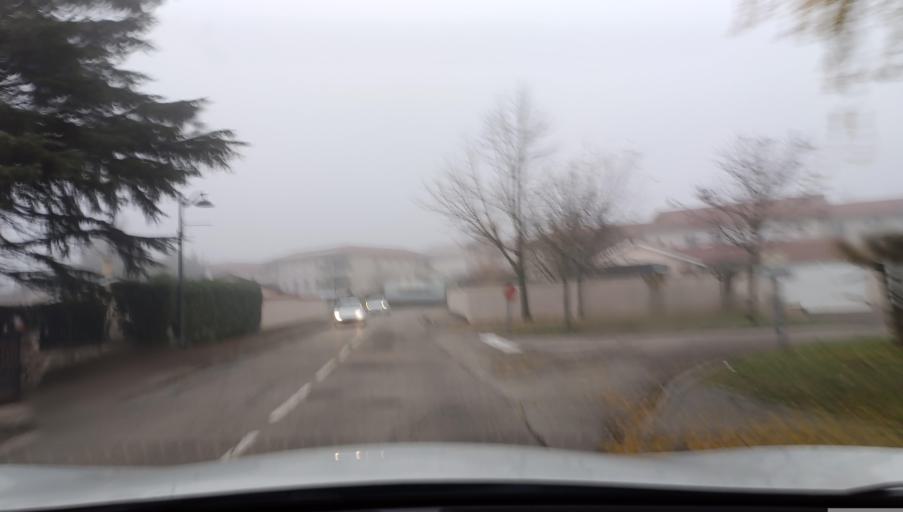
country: FR
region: Rhone-Alpes
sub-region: Departement de l'Isere
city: Serpaize
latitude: 45.5575
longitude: 4.9208
